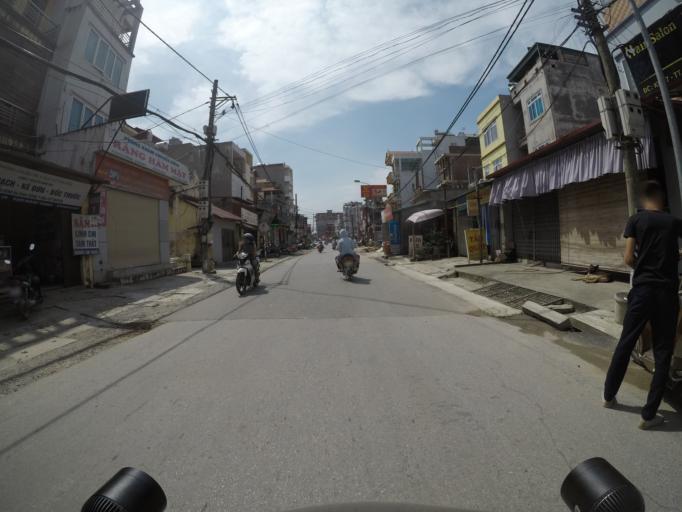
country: VN
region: Ha Noi
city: Troi
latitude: 21.0709
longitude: 105.7081
